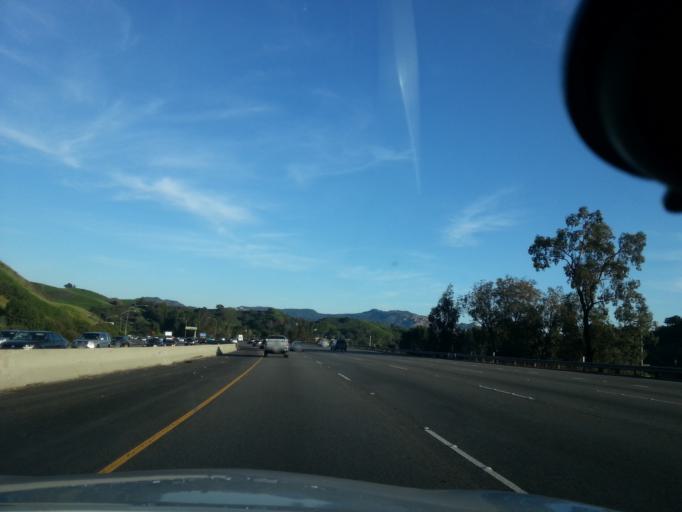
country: US
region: California
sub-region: Los Angeles County
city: Agoura
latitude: 34.1391
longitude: -118.7308
